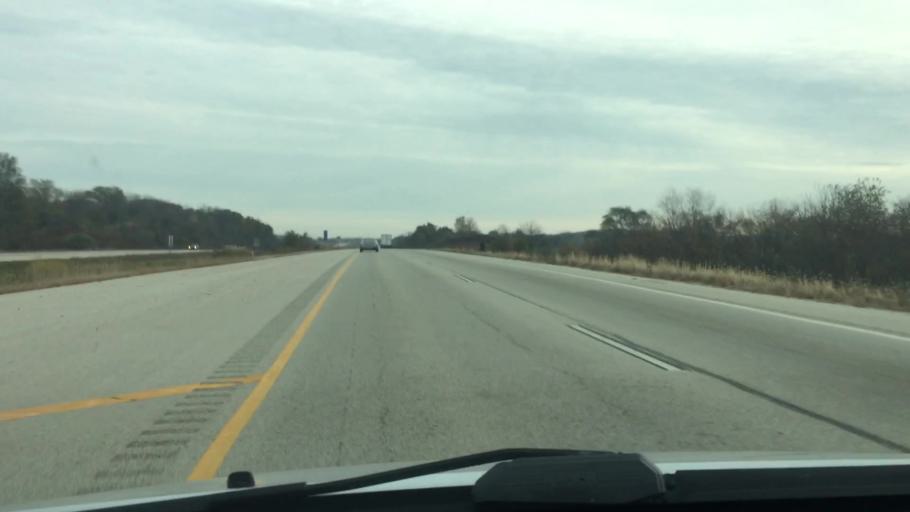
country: US
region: Wisconsin
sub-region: Waukesha County
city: Mukwonago
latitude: 42.8863
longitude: -88.2726
